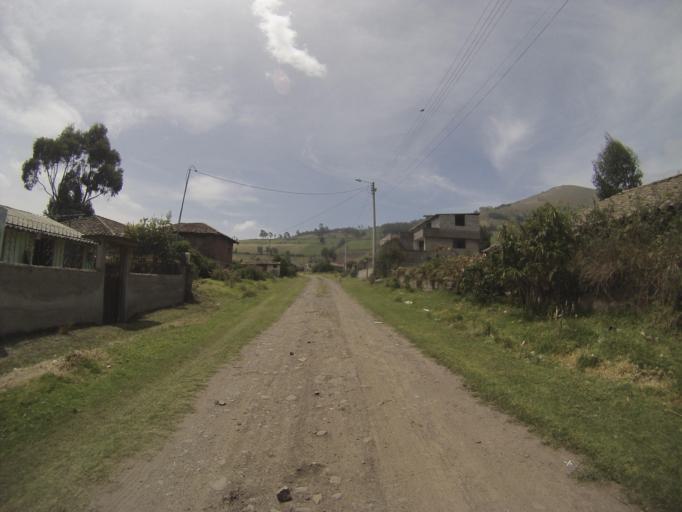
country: EC
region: Pichincha
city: Cayambe
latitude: 0.1512
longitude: -78.0674
